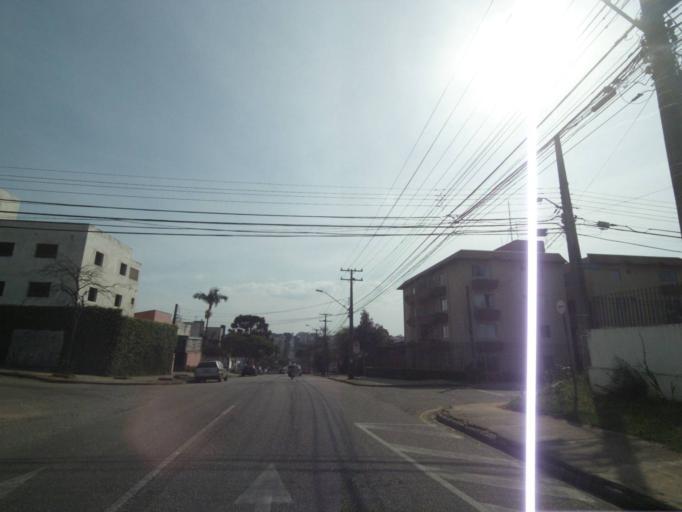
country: BR
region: Parana
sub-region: Curitiba
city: Curitiba
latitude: -25.4572
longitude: -49.3110
